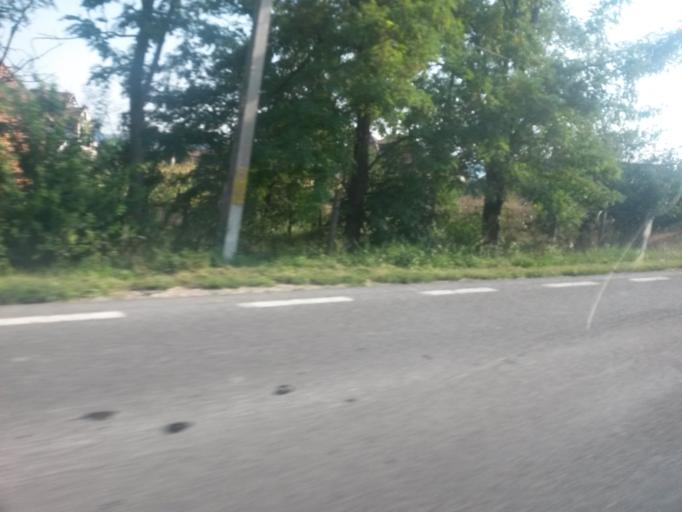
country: RO
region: Alba
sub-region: Comuna Unirea
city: Unirea
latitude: 46.3958
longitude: 23.8060
